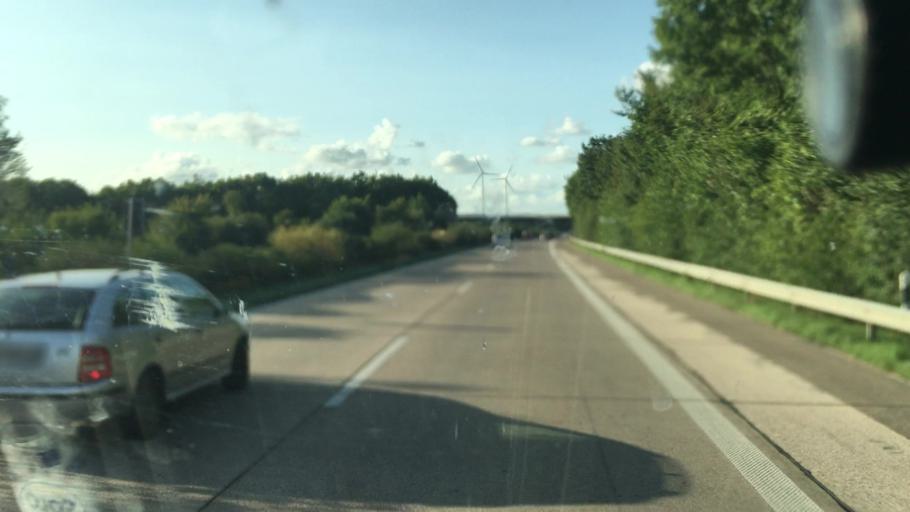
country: DE
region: Lower Saxony
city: Sande
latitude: 53.4889
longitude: 8.0027
